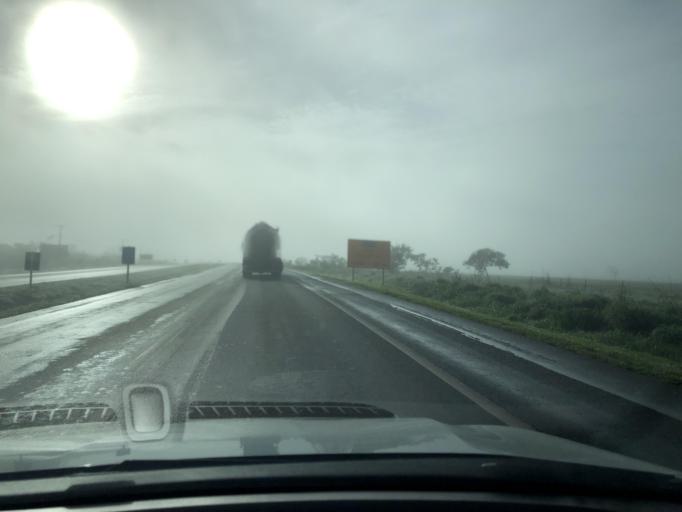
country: BR
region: Goias
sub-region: Luziania
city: Luziania
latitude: -16.2660
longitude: -47.8889
